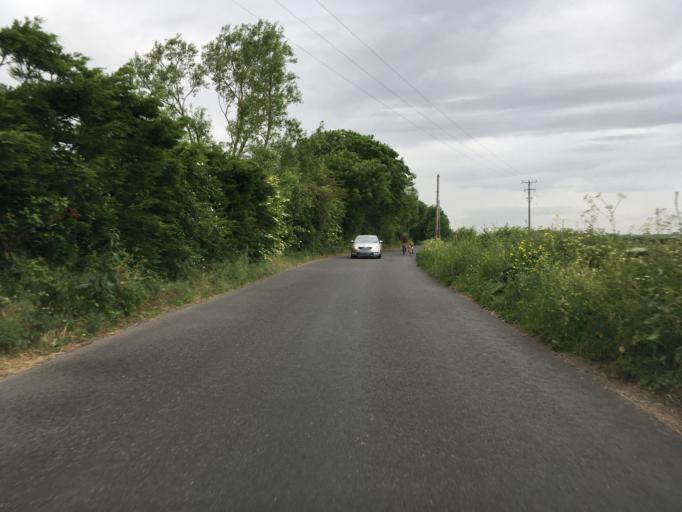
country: GB
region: England
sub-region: North Somerset
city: Kenn
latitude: 51.4234
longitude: -2.8183
